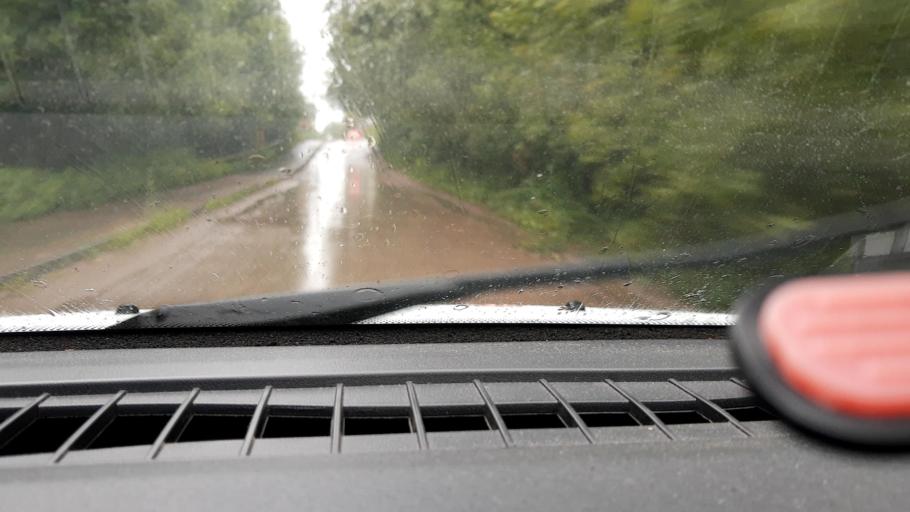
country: RU
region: Nizjnij Novgorod
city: Lyskovo
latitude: 56.0296
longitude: 45.0243
